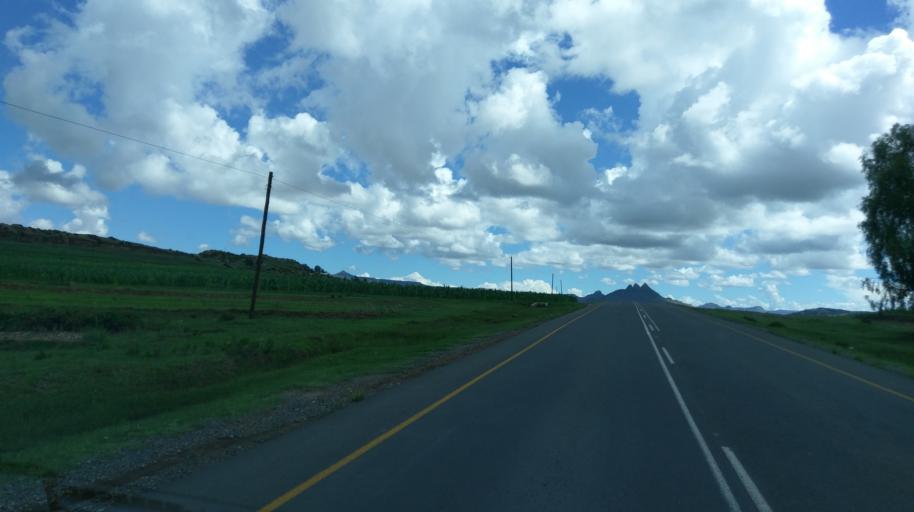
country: LS
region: Mafeteng
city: Mafeteng
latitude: -29.6776
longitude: 27.4467
